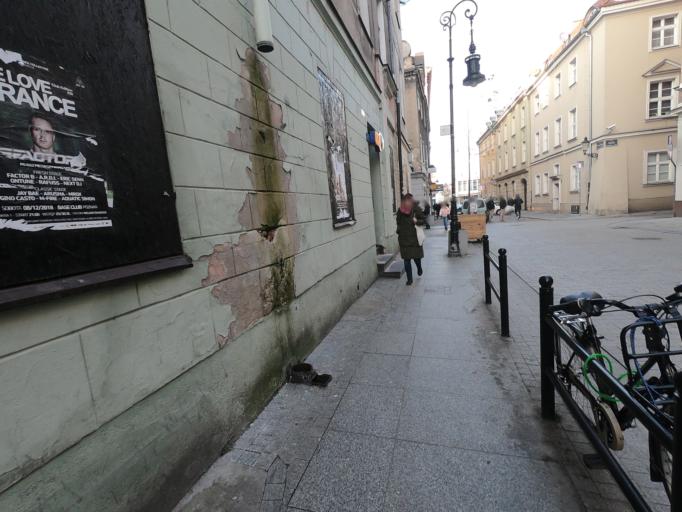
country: PL
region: Greater Poland Voivodeship
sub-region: Poznan
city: Poznan
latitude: 52.4070
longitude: 16.9332
